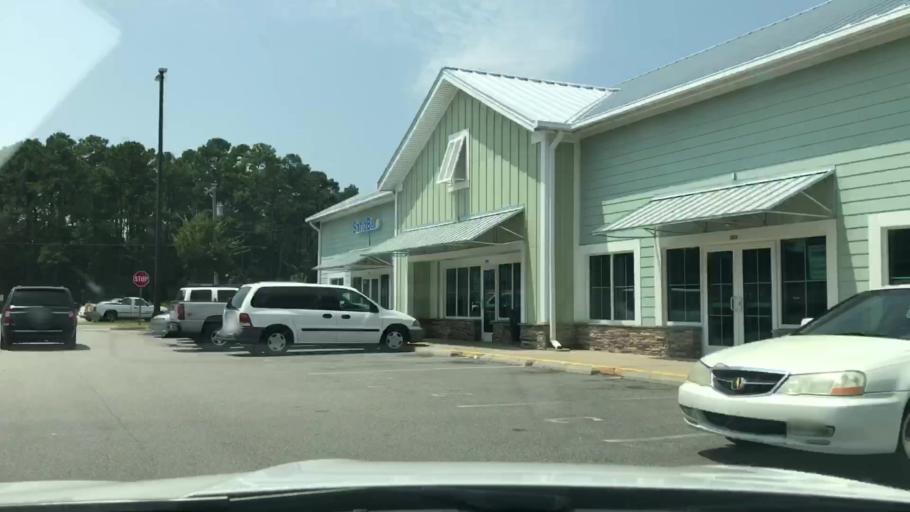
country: US
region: South Carolina
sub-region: Georgetown County
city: Murrells Inlet
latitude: 33.4370
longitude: -79.1321
